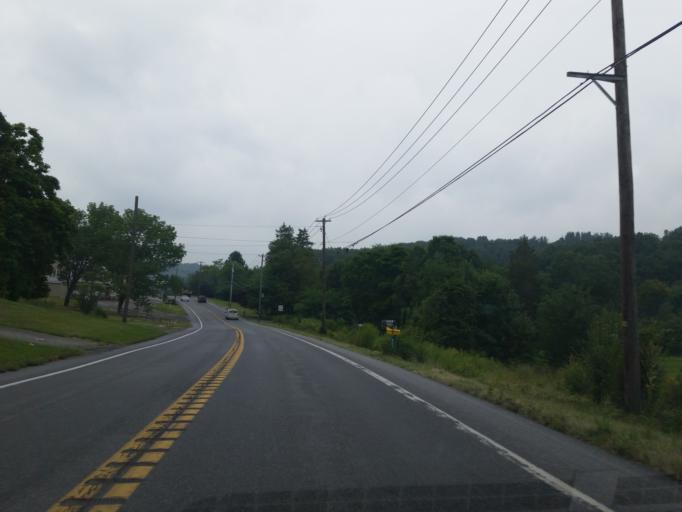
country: US
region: Pennsylvania
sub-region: Lancaster County
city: Brickerville
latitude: 40.2684
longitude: -76.3041
